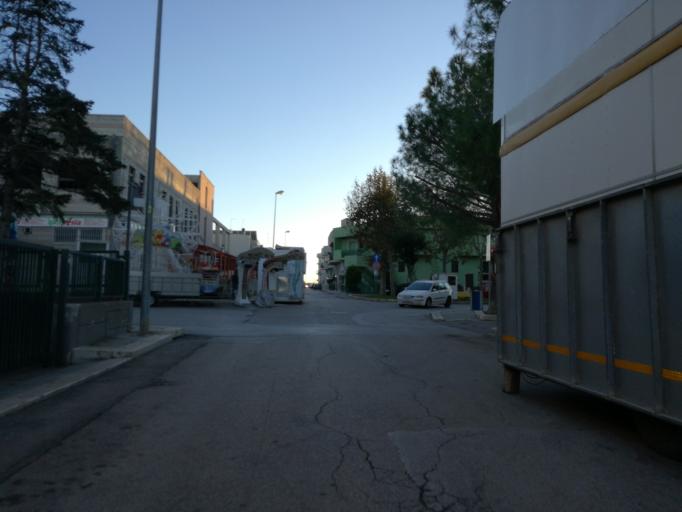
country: IT
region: Apulia
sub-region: Provincia di Bari
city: Adelfia
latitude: 41.0005
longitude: 16.8796
